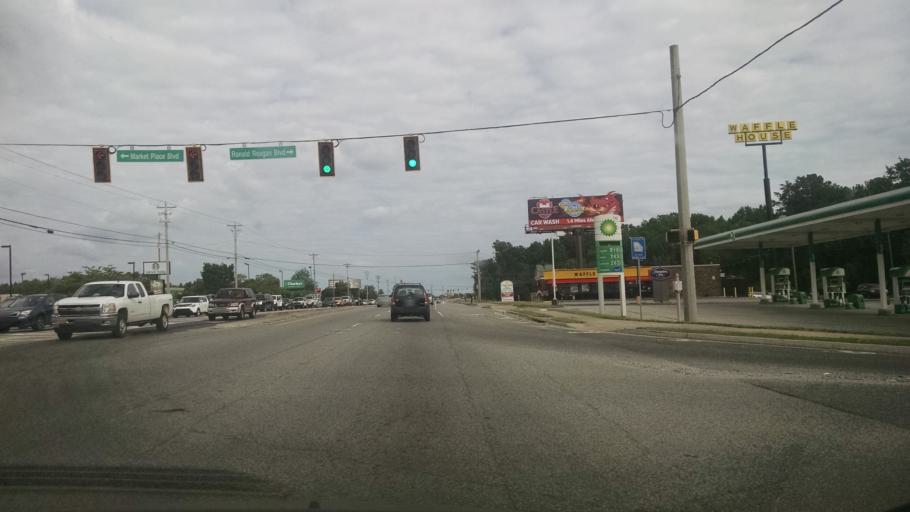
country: US
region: Georgia
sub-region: Forsyth County
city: Cumming
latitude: 34.1800
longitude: -84.1339
